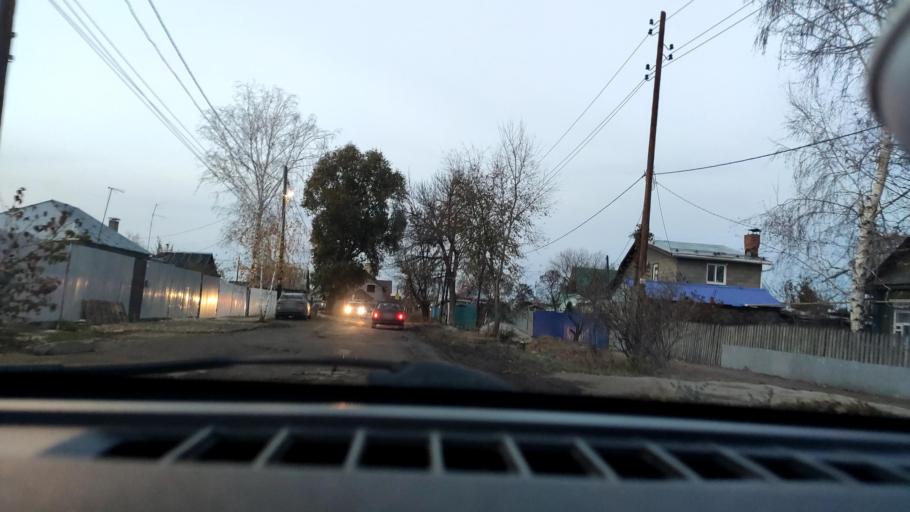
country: RU
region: Samara
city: Samara
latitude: 53.1341
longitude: 50.0949
